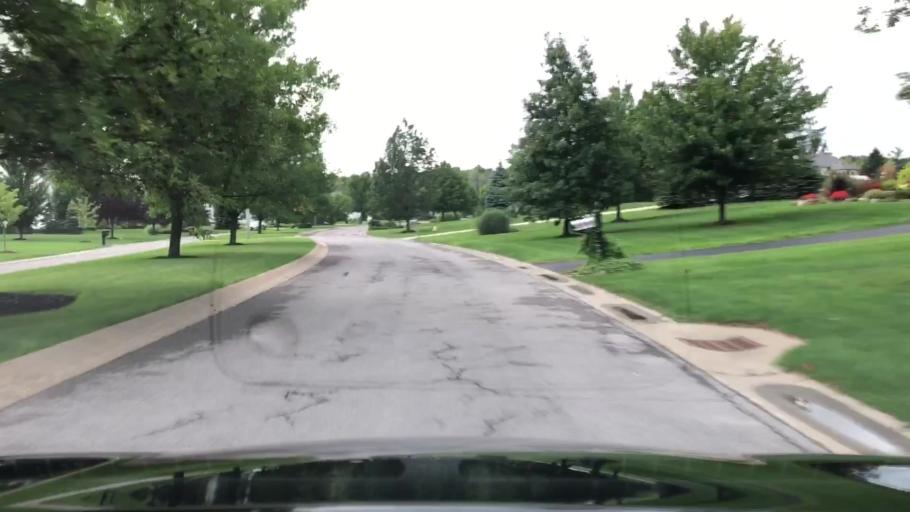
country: US
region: New York
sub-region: Erie County
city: Orchard Park
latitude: 42.7531
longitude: -78.7183
